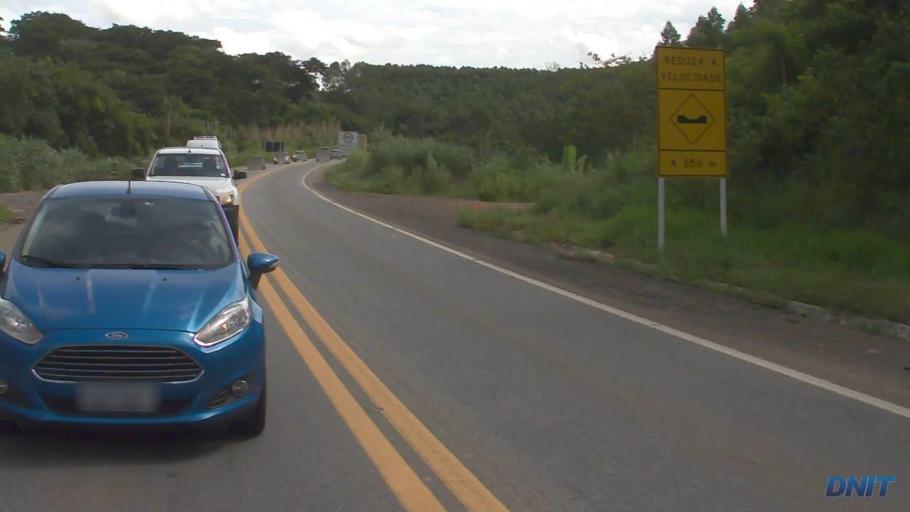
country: BR
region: Minas Gerais
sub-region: Ipaba
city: Ipaba
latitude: -19.3599
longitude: -42.4401
